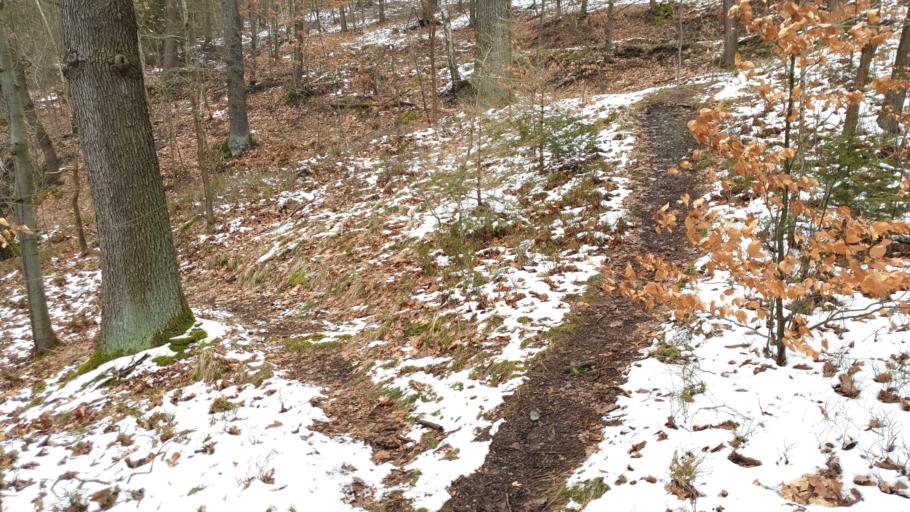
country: DE
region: Saxony
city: Gornau
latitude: 50.7725
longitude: 12.9801
